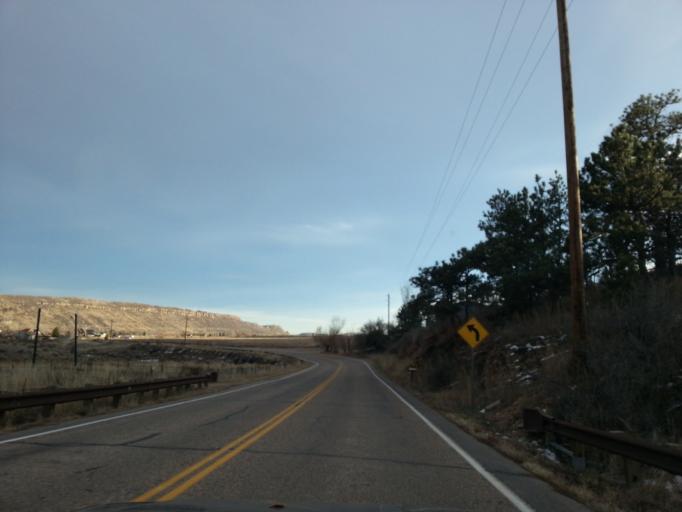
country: US
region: Colorado
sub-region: Larimer County
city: Loveland
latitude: 40.4704
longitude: -105.2112
